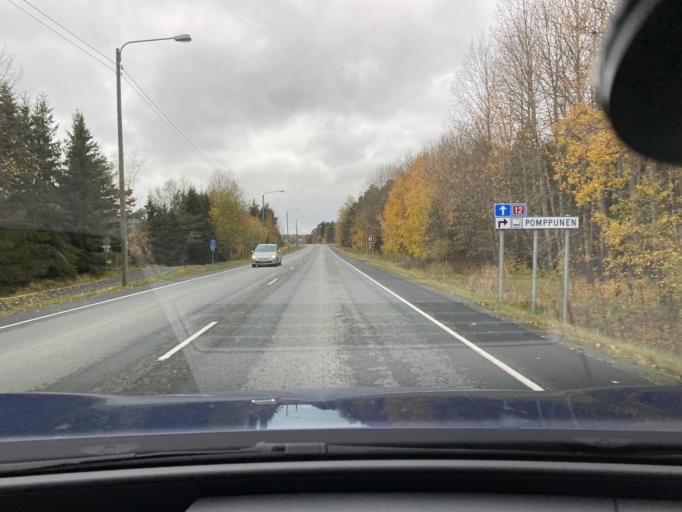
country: FI
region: Satakunta
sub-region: Rauma
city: Rauma
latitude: 61.1354
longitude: 21.5696
